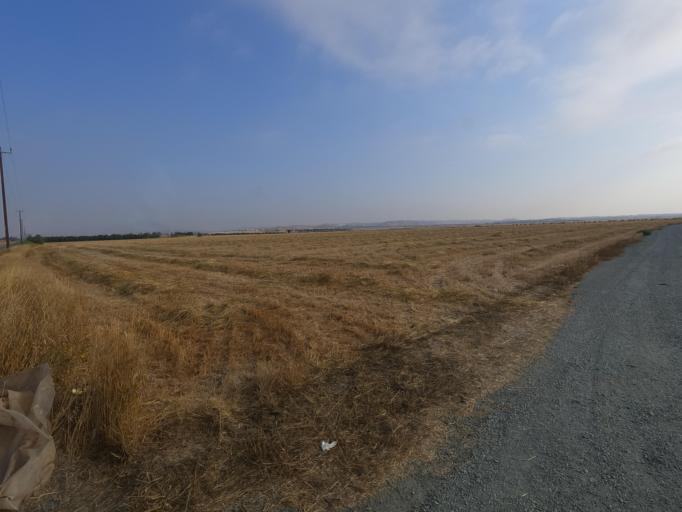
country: CY
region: Larnaka
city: Tersefanou
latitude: 34.8184
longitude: 33.5263
